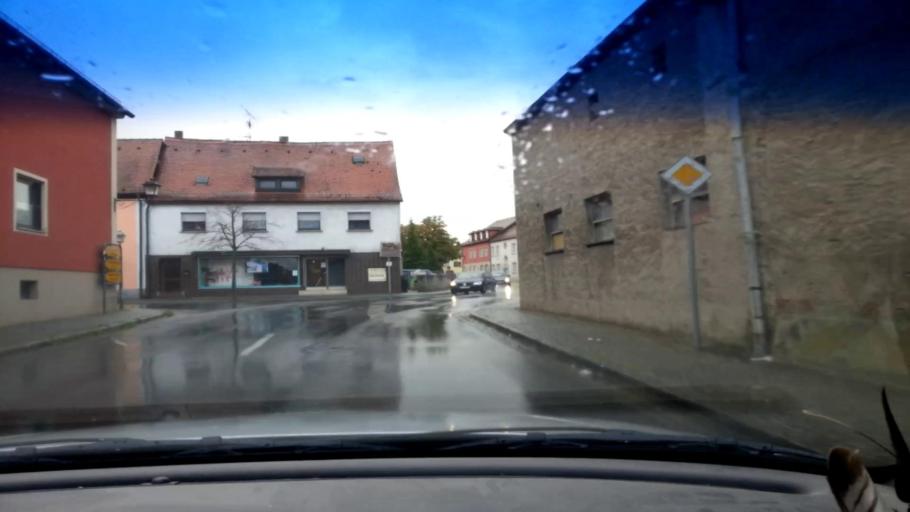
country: DE
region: Bavaria
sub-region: Upper Franconia
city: Burgebrach
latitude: 49.8289
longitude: 10.7423
